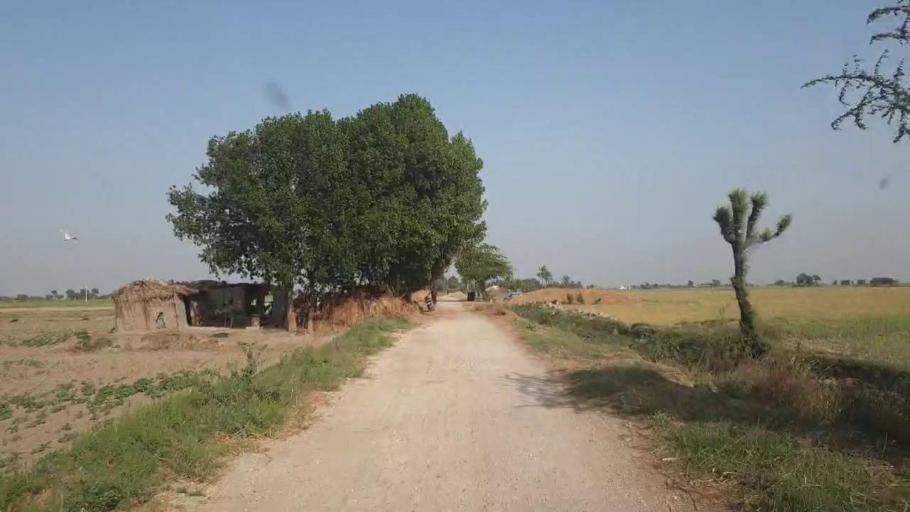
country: PK
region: Sindh
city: Kario
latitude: 24.5998
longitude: 68.5411
